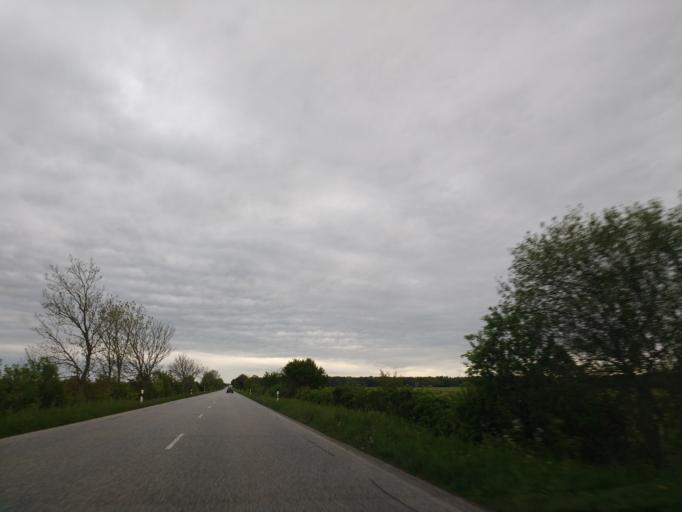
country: DE
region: Schleswig-Holstein
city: Dorphof
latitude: 54.6096
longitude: 9.9673
